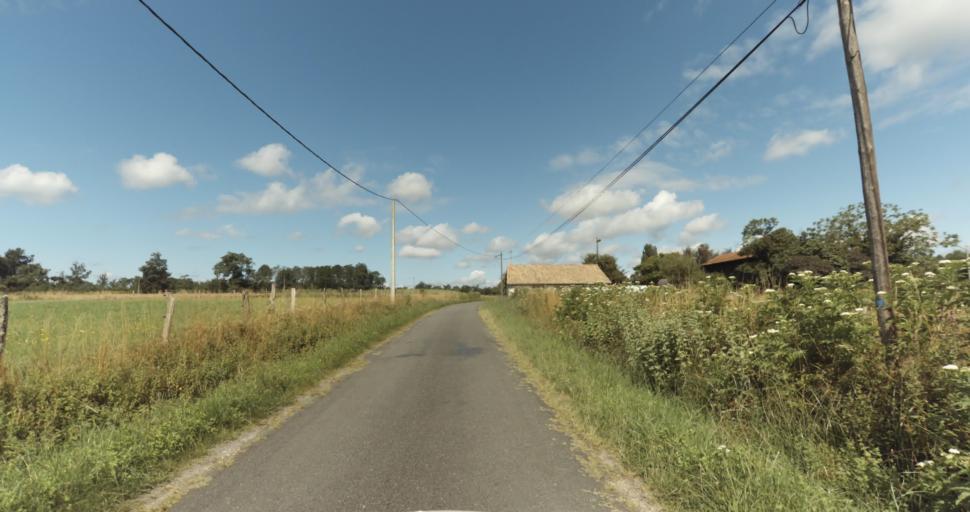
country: FR
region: Aquitaine
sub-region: Departement de la Gironde
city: Bazas
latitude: 44.4510
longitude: -0.2101
